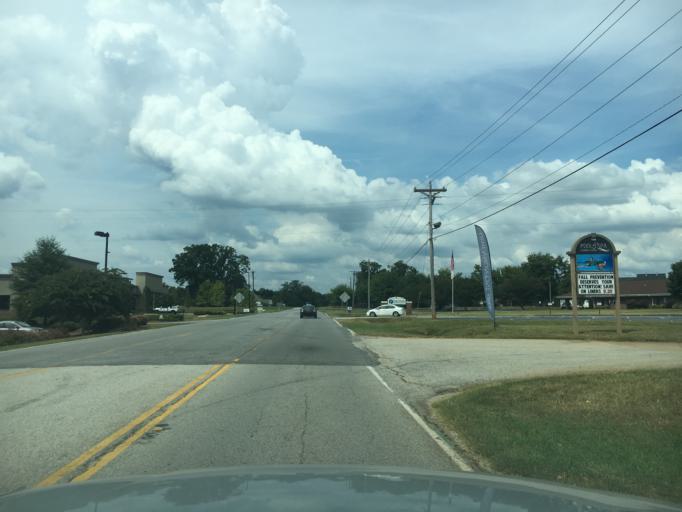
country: US
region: South Carolina
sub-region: Greenville County
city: Five Forks
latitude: 34.8078
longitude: -82.2323
